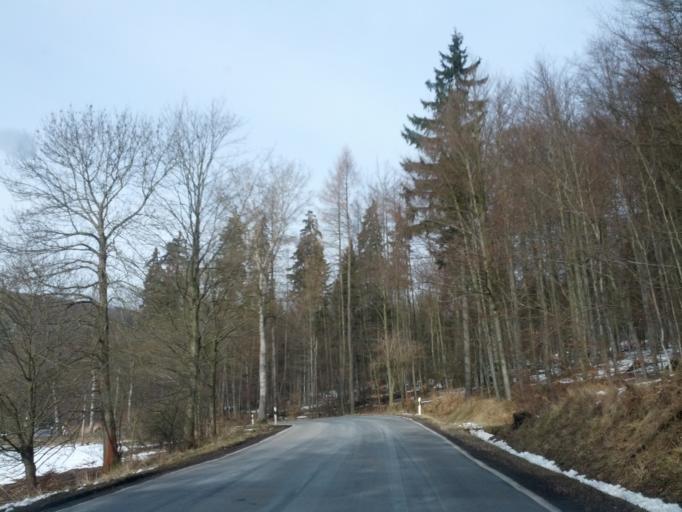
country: DE
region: Thuringia
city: Ruhla
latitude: 50.8747
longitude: 10.3767
